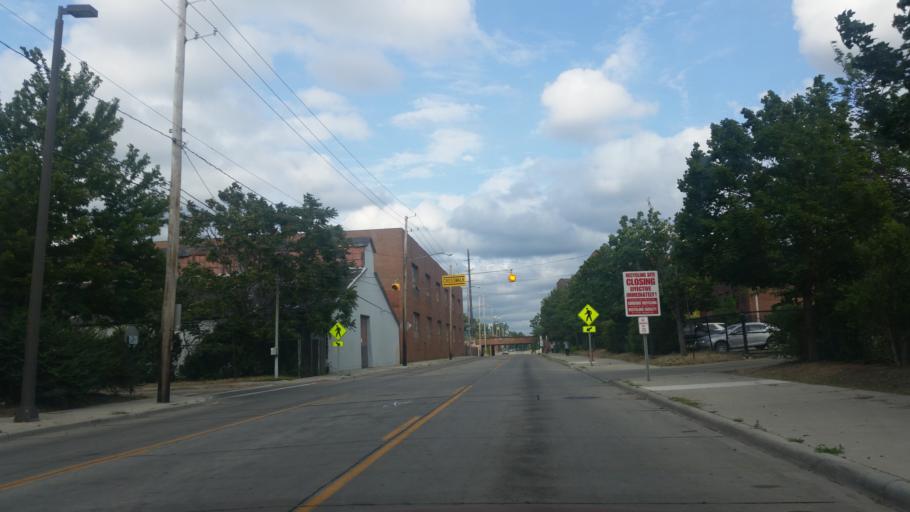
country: US
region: Ohio
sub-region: Cuyahoga County
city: Cleveland
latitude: 41.5005
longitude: -81.6502
